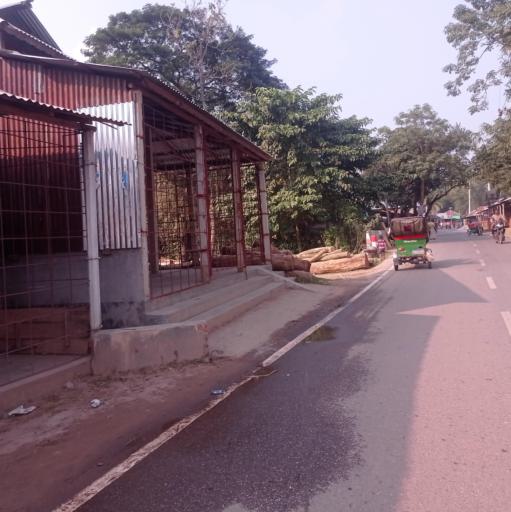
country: BD
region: Dhaka
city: Bhairab Bazar
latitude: 24.0819
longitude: 90.8492
